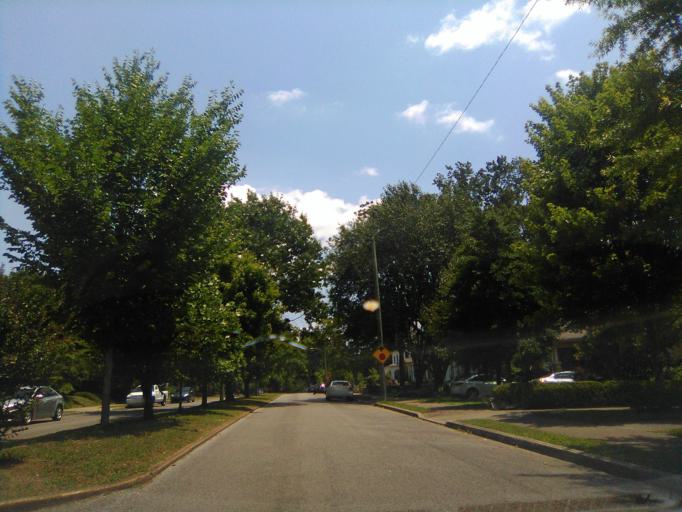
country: US
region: Tennessee
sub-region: Davidson County
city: Belle Meade
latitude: 36.1344
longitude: -86.8297
